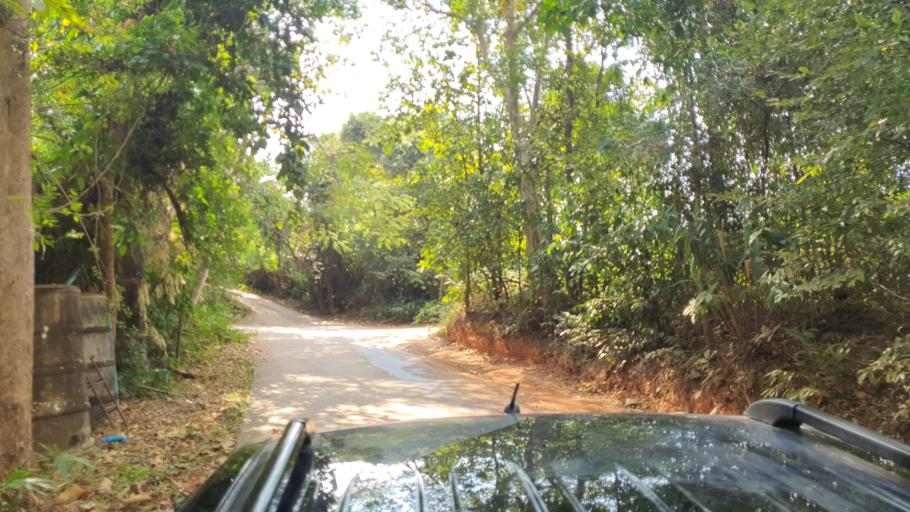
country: TH
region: Changwat Bueng Kan
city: Si Wilai
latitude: 18.2710
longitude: 103.7969
